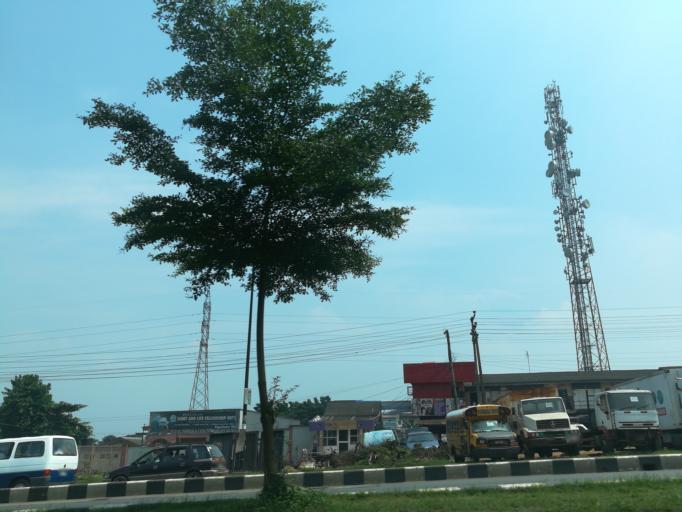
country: NG
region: Lagos
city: Ikorodu
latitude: 6.6252
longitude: 3.4890
